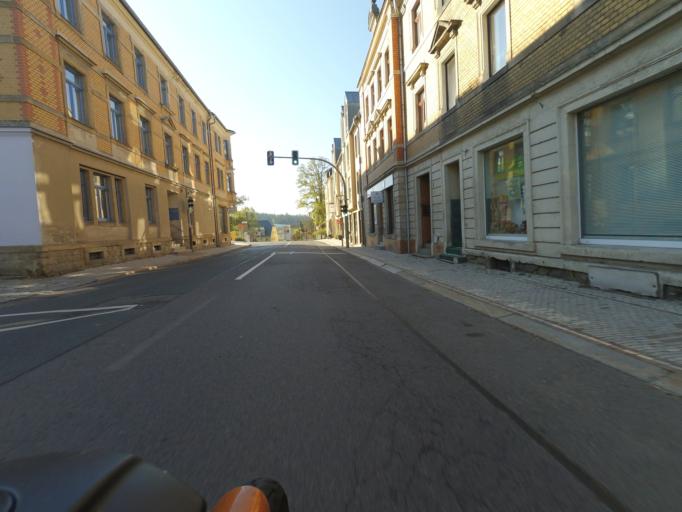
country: DE
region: Saxony
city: Rabenau
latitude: 50.9638
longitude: 13.6417
